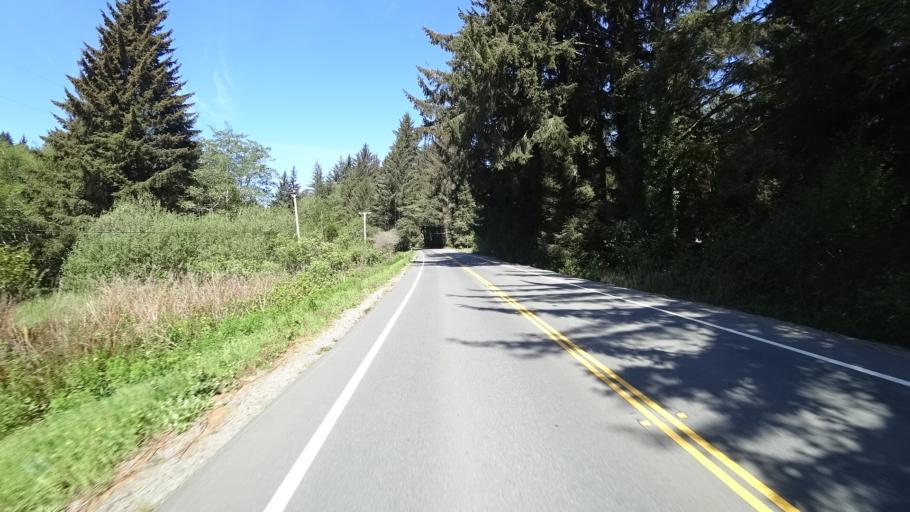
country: US
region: California
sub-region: Del Norte County
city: Bertsch-Oceanview
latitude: 41.5818
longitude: -124.0801
